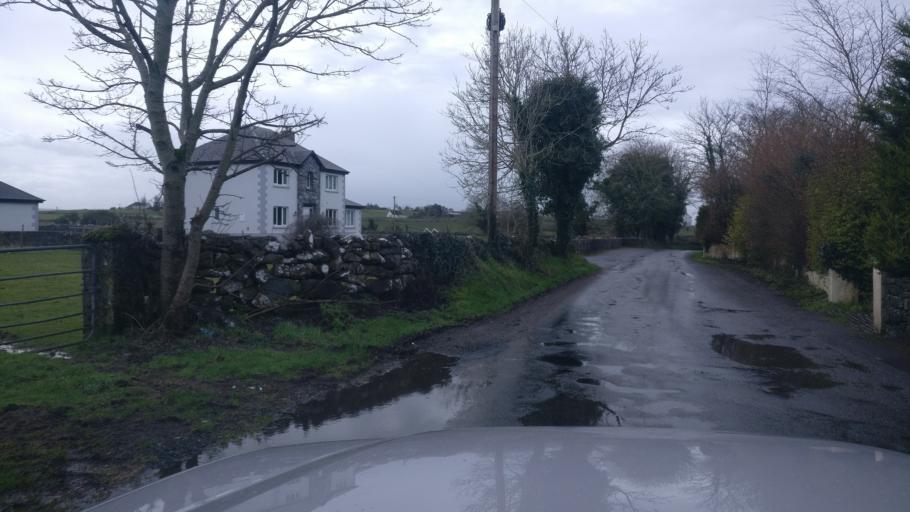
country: IE
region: Connaught
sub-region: County Galway
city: Loughrea
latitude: 53.2029
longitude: -8.5965
